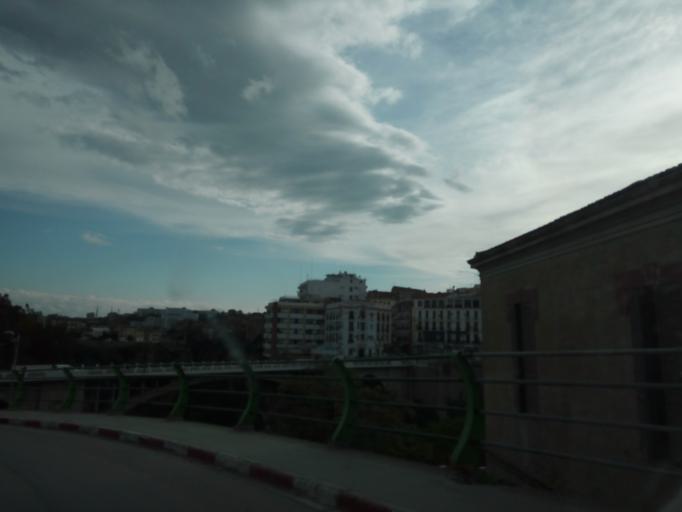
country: DZ
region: Constantine
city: Constantine
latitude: 36.3699
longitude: 6.6190
